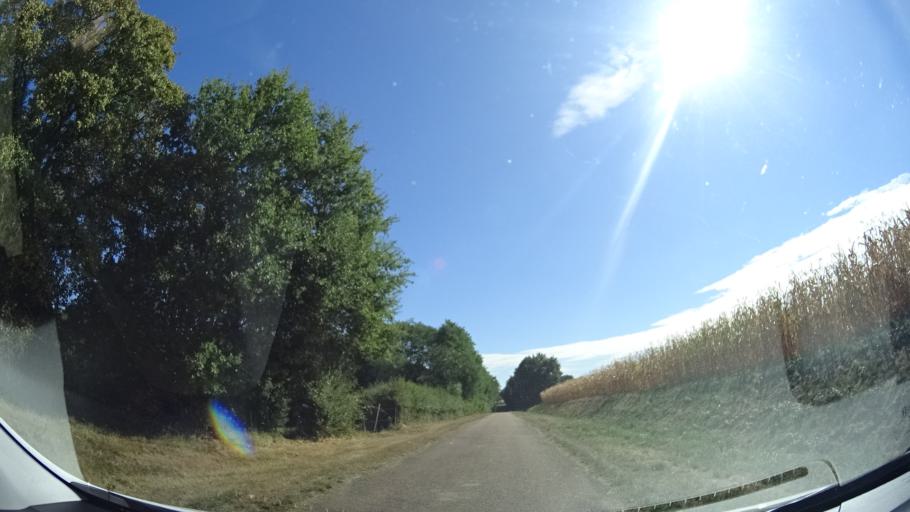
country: FR
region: Centre
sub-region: Departement du Loiret
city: Trigueres
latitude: 47.9435
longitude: 2.9511
